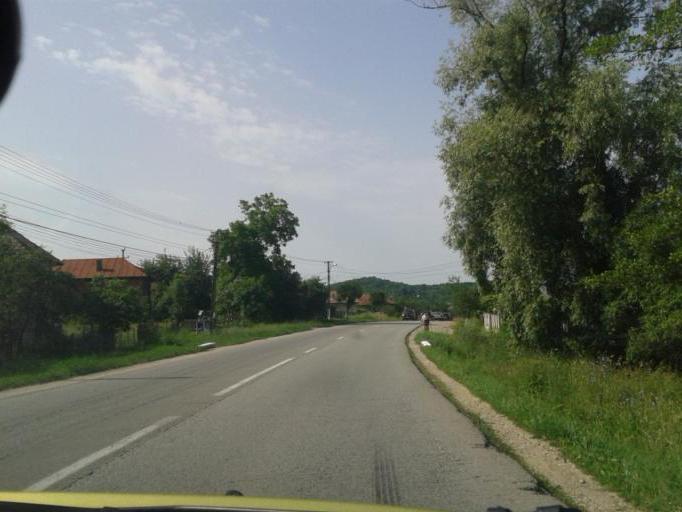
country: RO
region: Valcea
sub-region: Comuna Pietrari
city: Pietrarii de Sus
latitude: 45.1161
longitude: 24.1162
